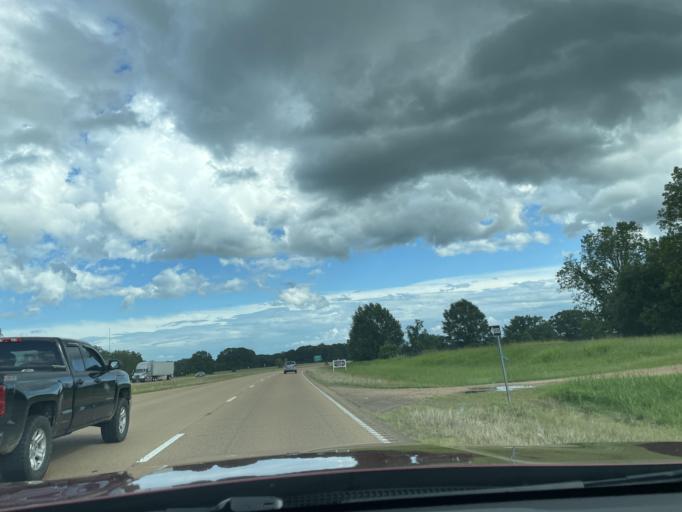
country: US
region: Mississippi
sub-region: Madison County
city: Flora
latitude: 32.5639
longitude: -90.3249
